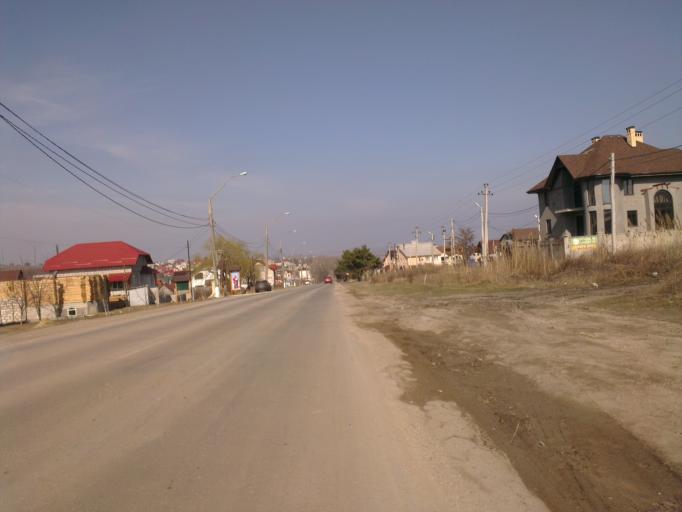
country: MD
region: Chisinau
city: Cricova
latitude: 47.1203
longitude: 28.8671
